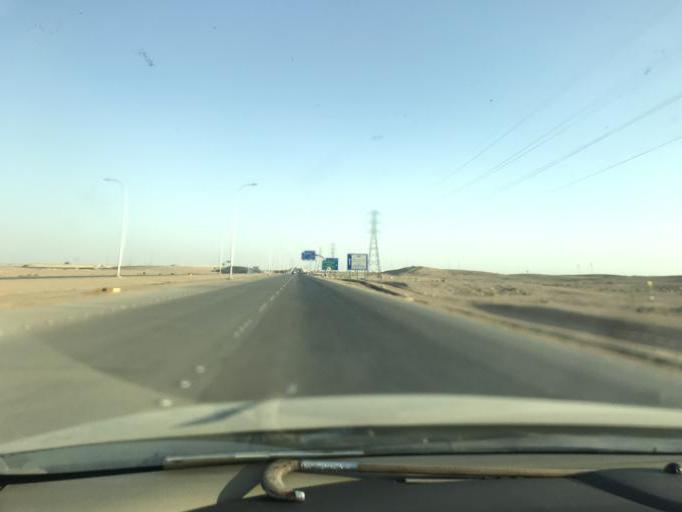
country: SA
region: Ar Riyad
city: Riyadh
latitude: 24.9110
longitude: 46.7007
